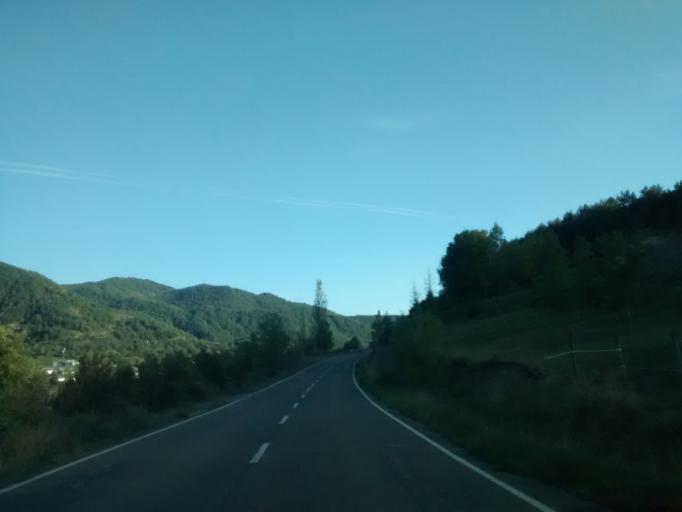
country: ES
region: Aragon
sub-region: Provincia de Huesca
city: Anso
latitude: 42.7486
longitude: -0.7503
